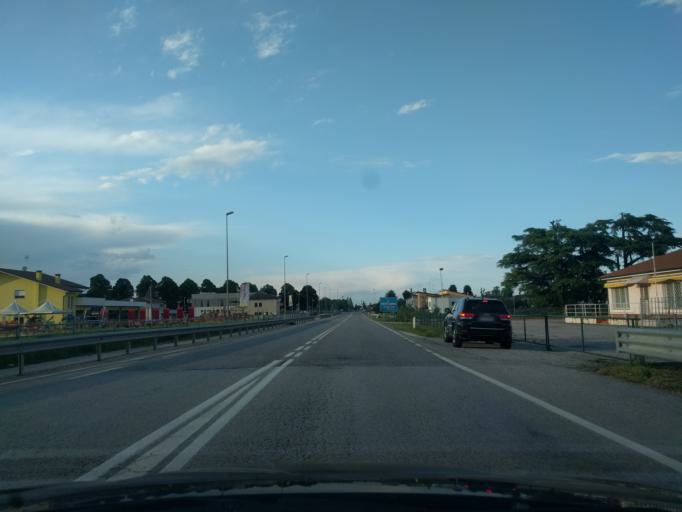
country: IT
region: Veneto
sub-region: Provincia di Rovigo
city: Polesella
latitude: 44.9586
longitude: 11.7398
